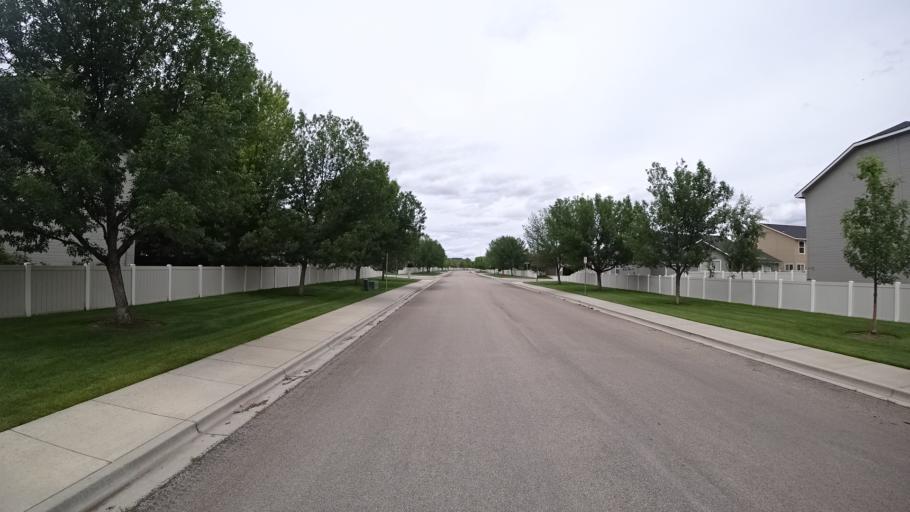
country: US
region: Idaho
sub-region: Ada County
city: Meridian
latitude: 43.6434
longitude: -116.4011
